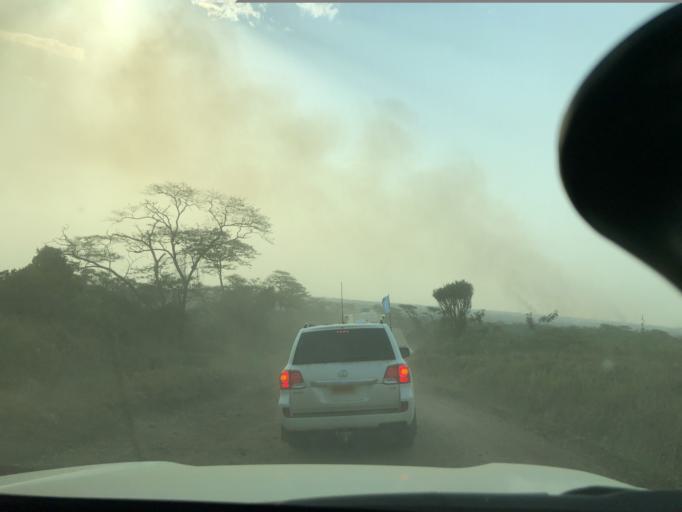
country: CD
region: Nord Kivu
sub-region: North Kivu
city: Butembo
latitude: 0.1449
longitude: 29.6421
